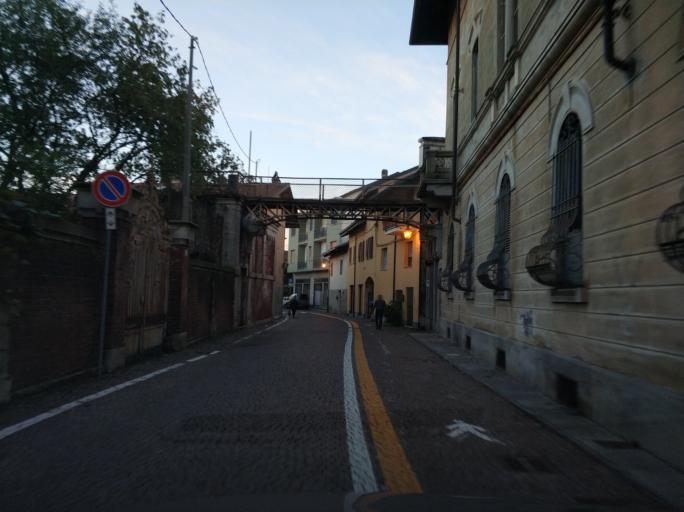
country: IT
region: Piedmont
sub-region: Provincia di Torino
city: Robassomero
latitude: 45.1990
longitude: 7.5728
